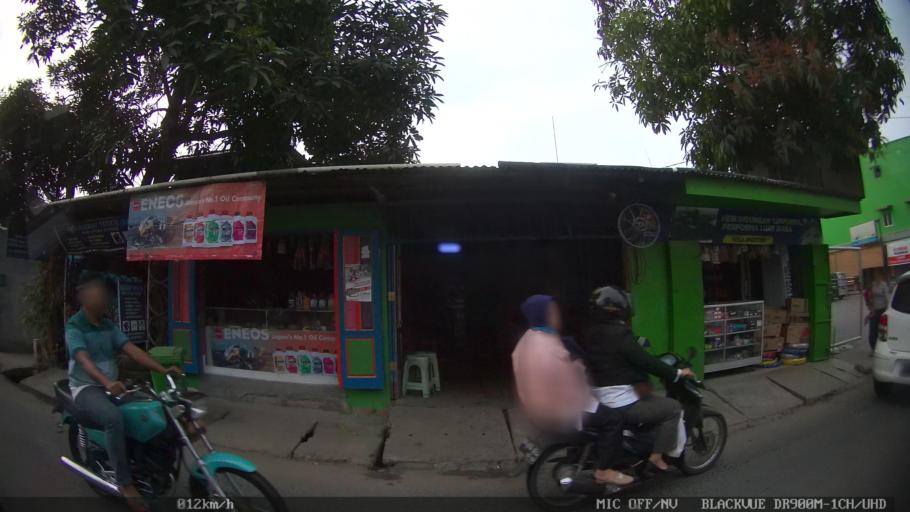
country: ID
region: North Sumatra
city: Sunggal
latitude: 3.5639
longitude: 98.6027
